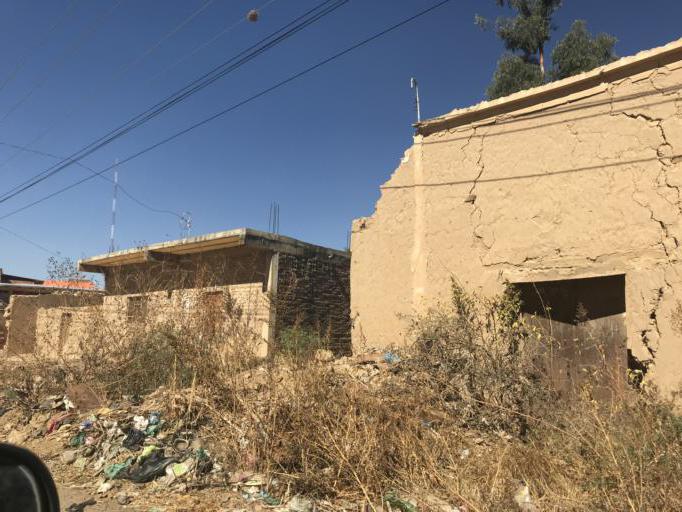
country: BO
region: Cochabamba
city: Cliza
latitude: -17.5936
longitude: -65.9426
